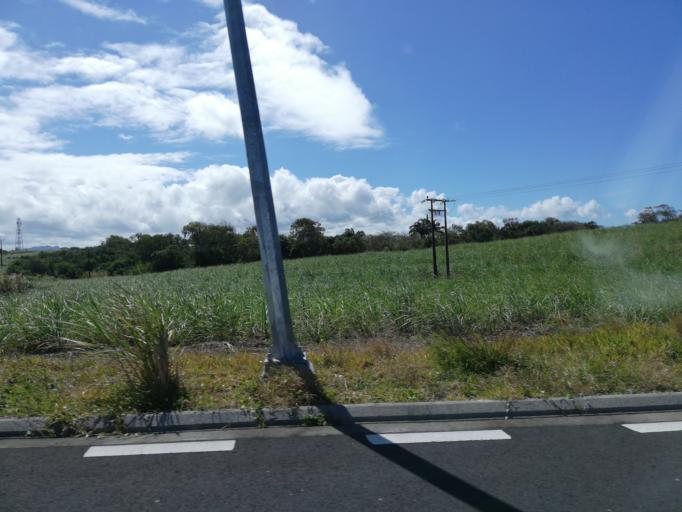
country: MU
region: Grand Port
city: Beau Vallon
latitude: -20.4501
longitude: 57.6954
